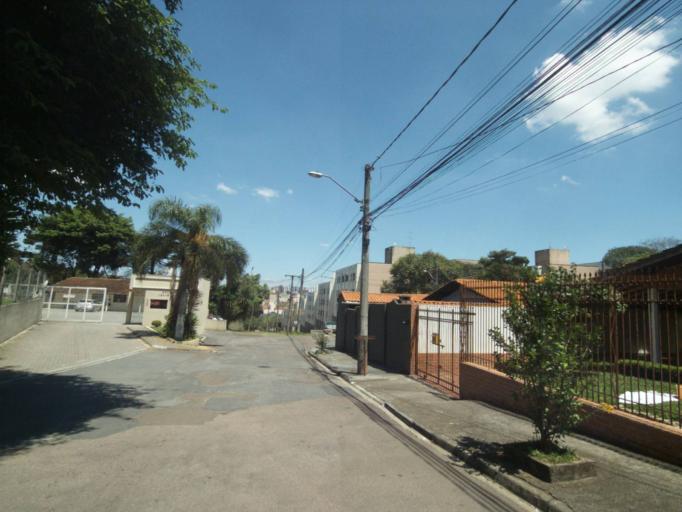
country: BR
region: Parana
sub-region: Curitiba
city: Curitiba
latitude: -25.3865
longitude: -49.2311
